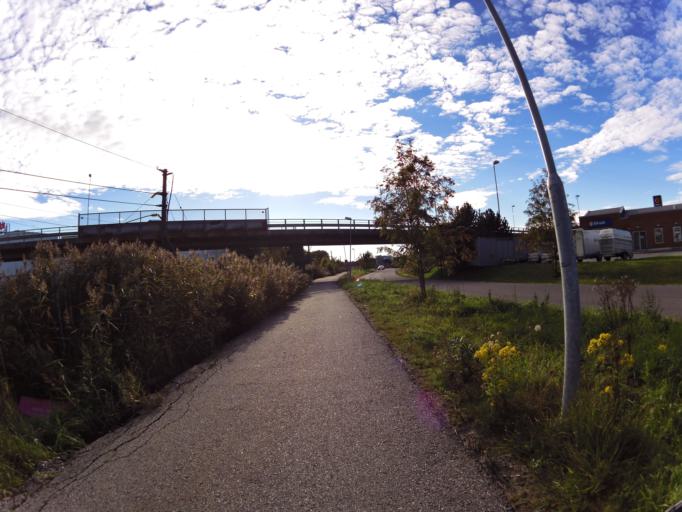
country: NO
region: Ostfold
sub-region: Sarpsborg
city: Sarpsborg
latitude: 59.2745
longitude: 11.0874
